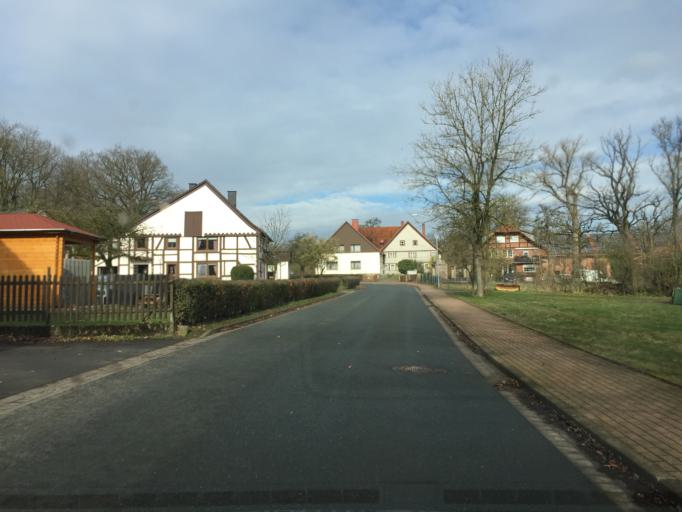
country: DE
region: Lower Saxony
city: Aerzen
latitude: 52.0798
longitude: 9.1855
